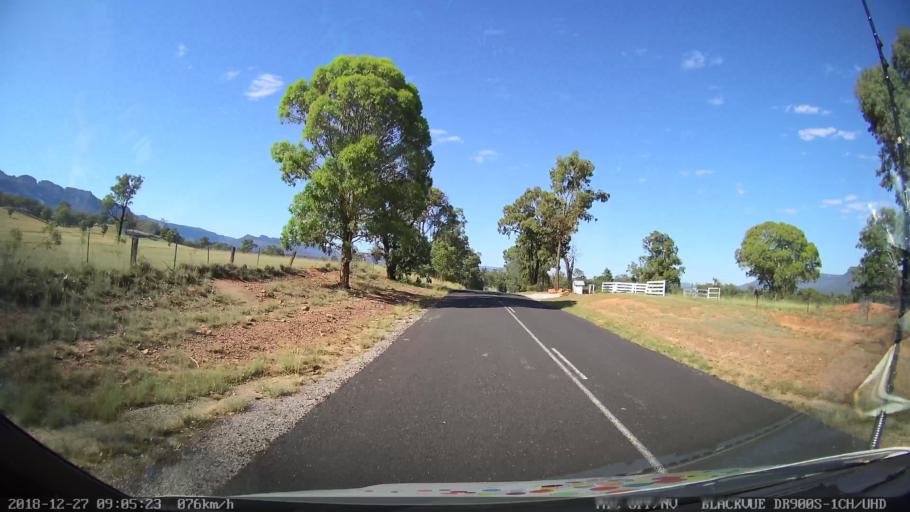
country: AU
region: New South Wales
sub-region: Lithgow
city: Portland
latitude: -33.1169
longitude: 150.1806
